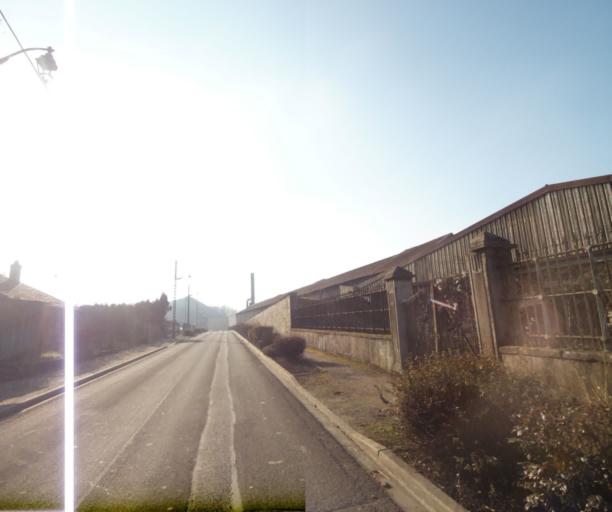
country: FR
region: Champagne-Ardenne
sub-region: Departement de la Haute-Marne
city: Wassy
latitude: 48.4892
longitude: 4.9689
